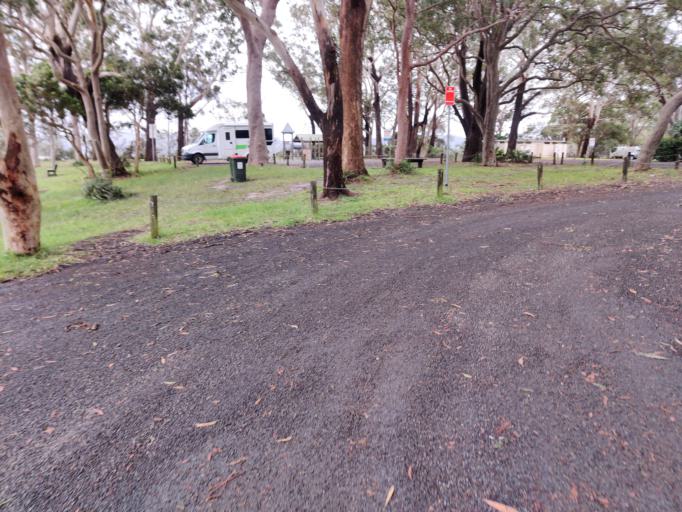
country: AU
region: New South Wales
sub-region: Great Lakes
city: Forster
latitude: -32.3902
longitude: 152.5021
